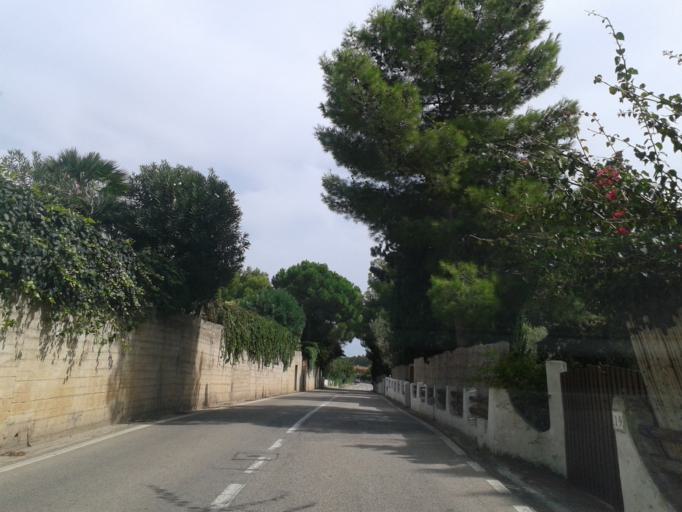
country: IT
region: Sardinia
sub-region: Provincia di Cagliari
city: Villasimius
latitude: 39.1315
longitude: 9.5064
